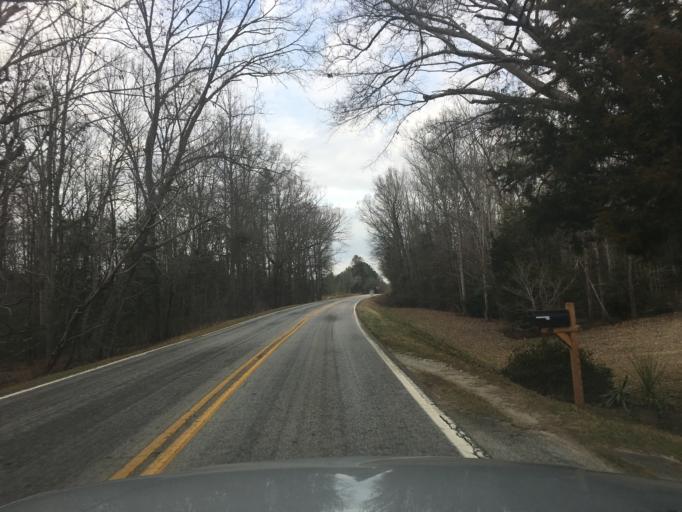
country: US
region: South Carolina
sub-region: Abbeville County
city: Due West
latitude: 34.2916
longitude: -82.4471
